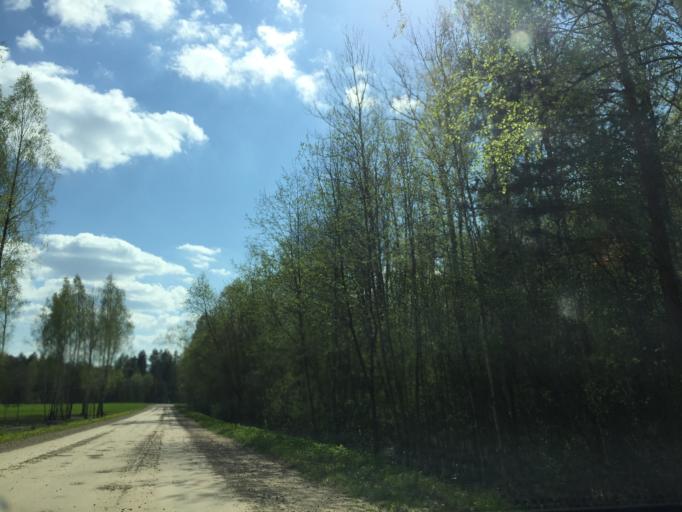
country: LV
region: Vecumnieki
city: Vecumnieki
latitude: 56.4784
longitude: 24.5326
